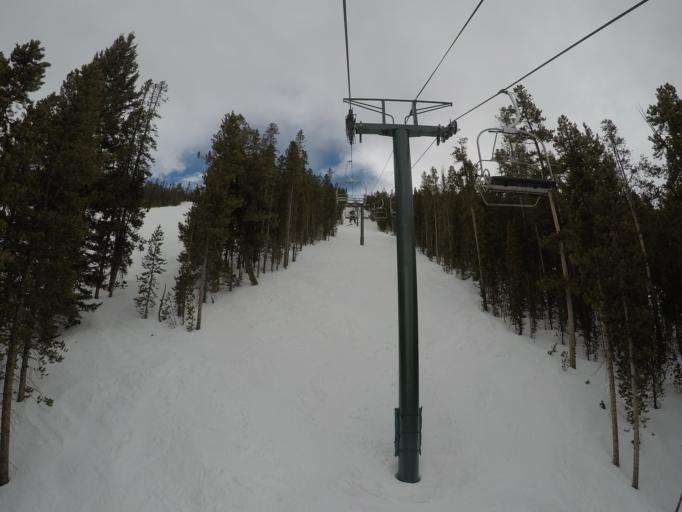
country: US
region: Montana
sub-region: Granite County
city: Philipsburg
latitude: 46.2564
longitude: -113.2440
